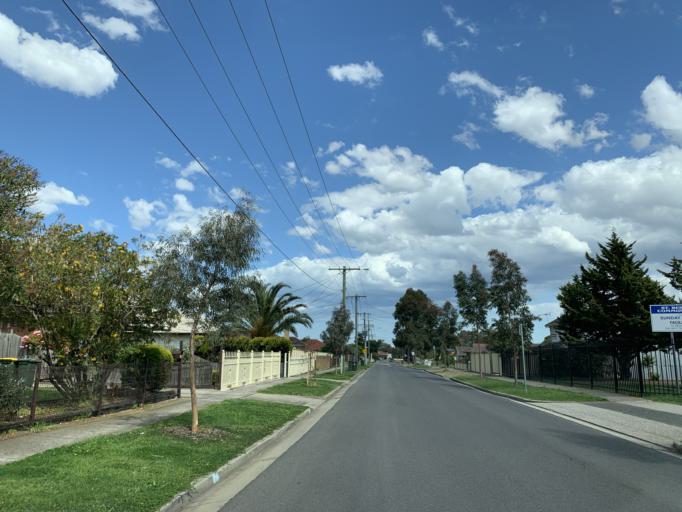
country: AU
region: Victoria
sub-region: Brimbank
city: Albion
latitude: -37.7592
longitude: 144.8276
